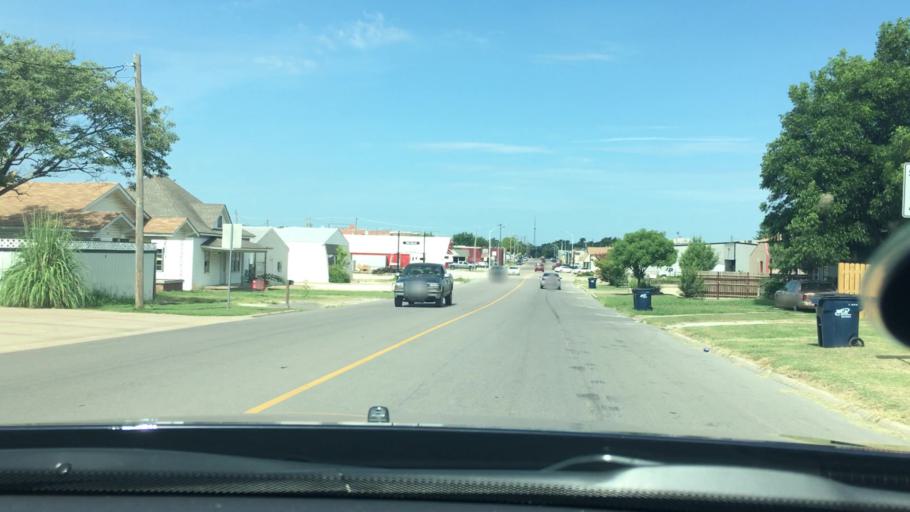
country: US
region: Oklahoma
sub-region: Pontotoc County
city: Ada
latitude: 34.7756
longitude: -96.6723
